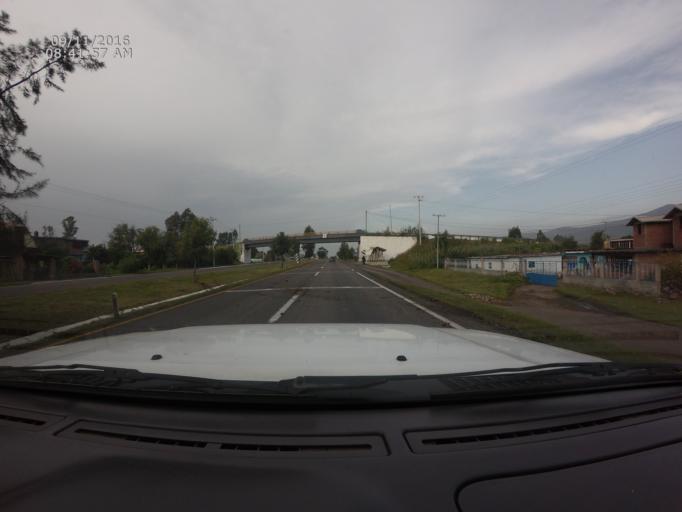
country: MX
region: Michoacan
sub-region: Morelia
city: La Mintzita (Piedra Dura)
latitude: 19.5948
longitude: -101.2956
